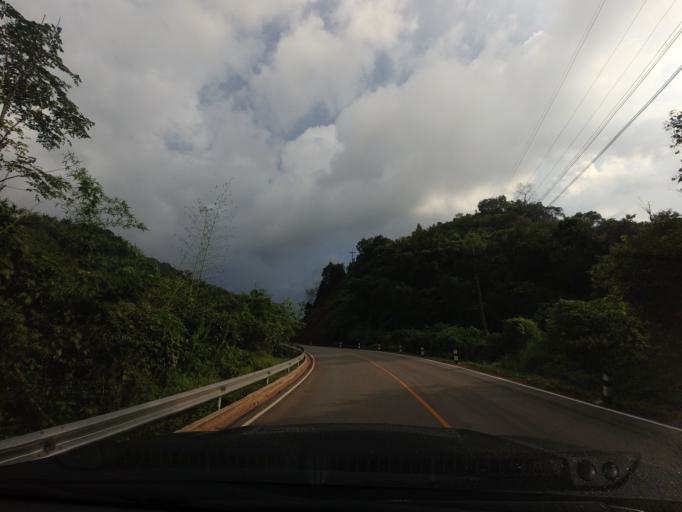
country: TH
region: Nan
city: Bo Kluea
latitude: 19.2655
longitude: 101.1783
